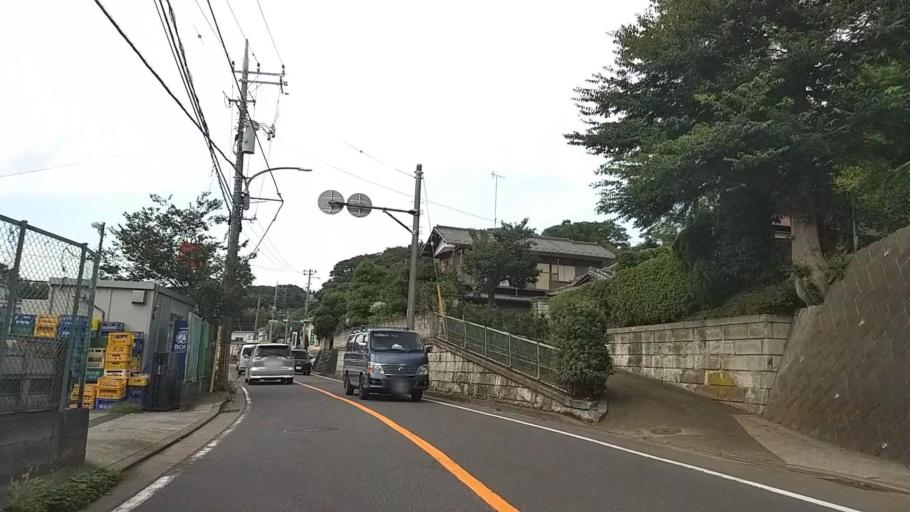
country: JP
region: Kanagawa
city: Yokohama
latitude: 35.4906
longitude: 139.5708
